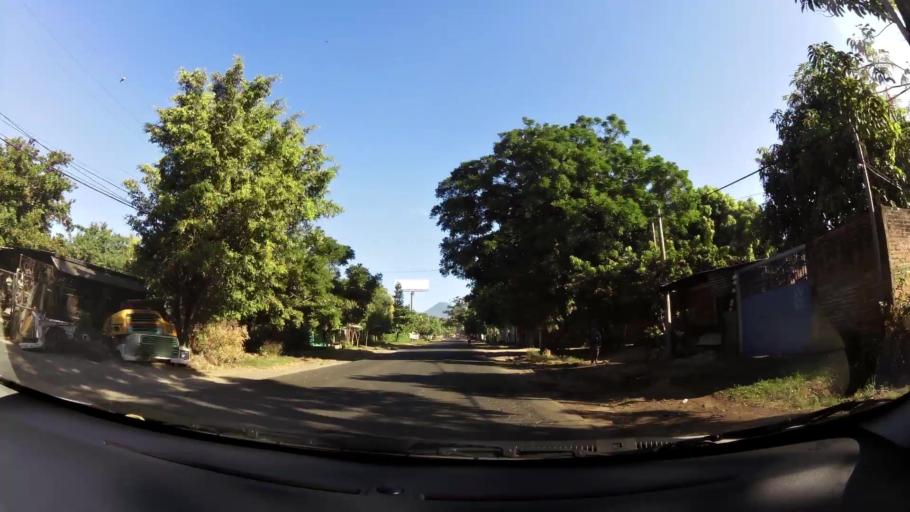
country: SV
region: Sonsonate
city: Sonzacate
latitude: 13.7400
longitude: -89.7094
